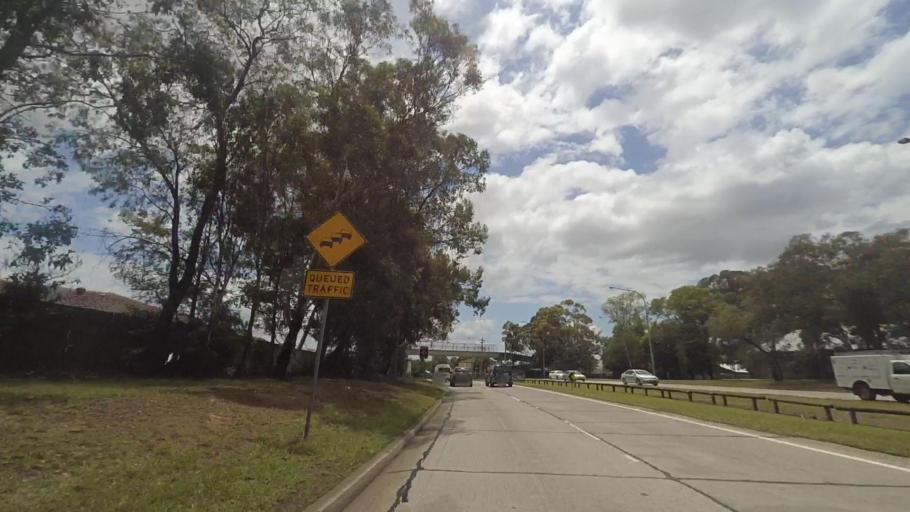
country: AU
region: New South Wales
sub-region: Fairfield
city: Cabramatta West
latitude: -33.8969
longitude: 150.9213
